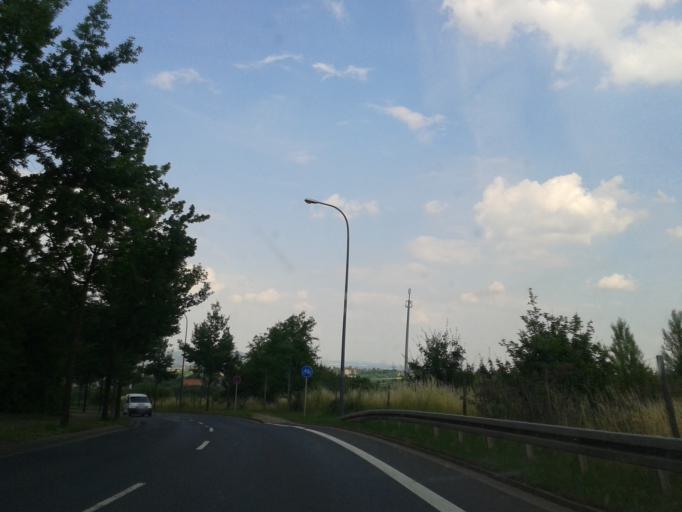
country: DE
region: Saxony
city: Bannewitz
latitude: 51.0136
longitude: 13.7120
